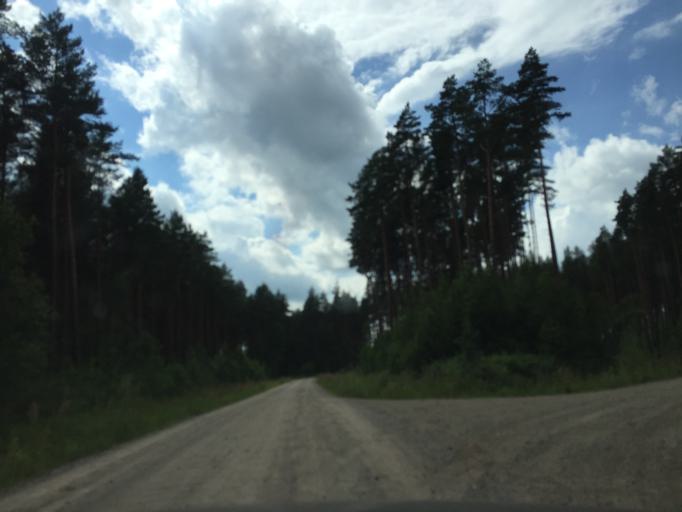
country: LV
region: Jelgava
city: Jelgava
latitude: 56.6261
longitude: 23.6297
